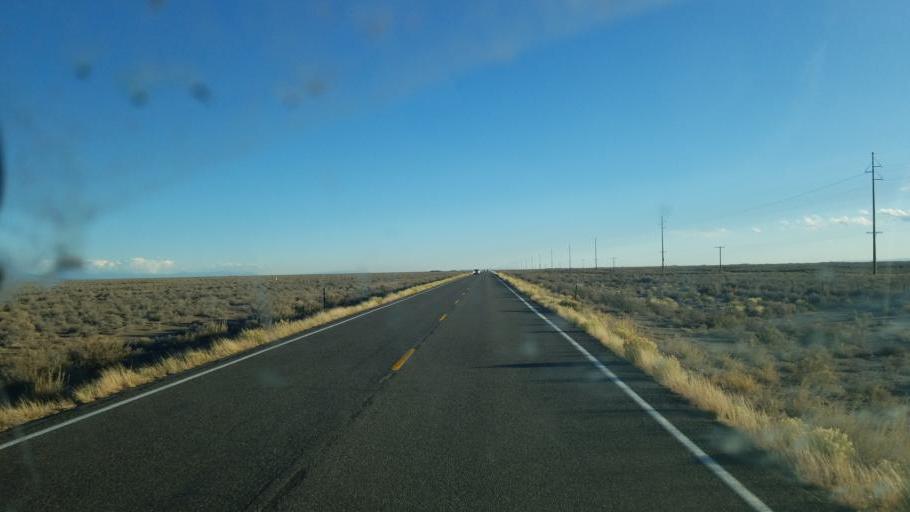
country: US
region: Colorado
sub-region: Saguache County
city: Center
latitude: 37.9018
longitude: -105.8976
